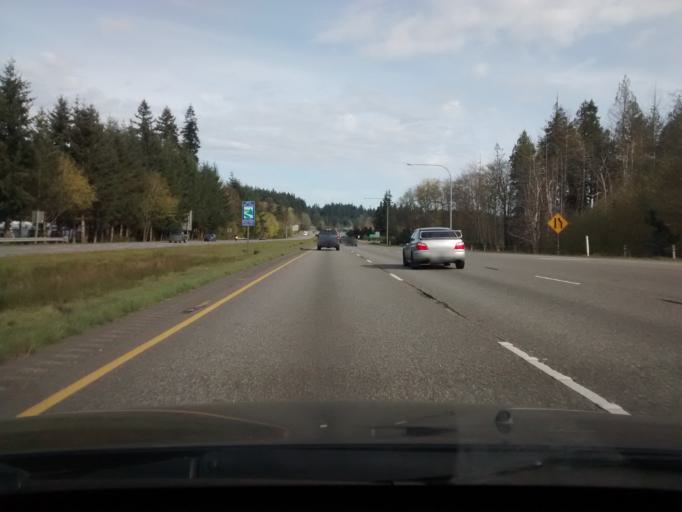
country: US
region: Washington
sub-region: Kitsap County
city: Silverdale
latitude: 47.6679
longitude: -122.6878
